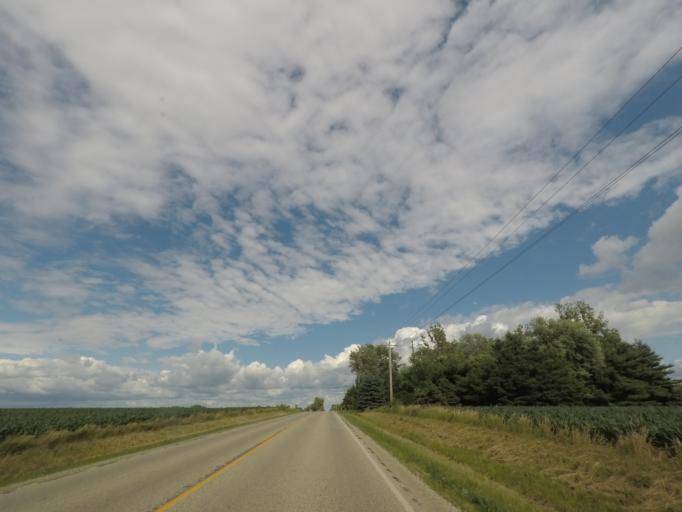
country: US
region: Wisconsin
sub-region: Rock County
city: Janesville
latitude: 42.7012
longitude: -89.1198
